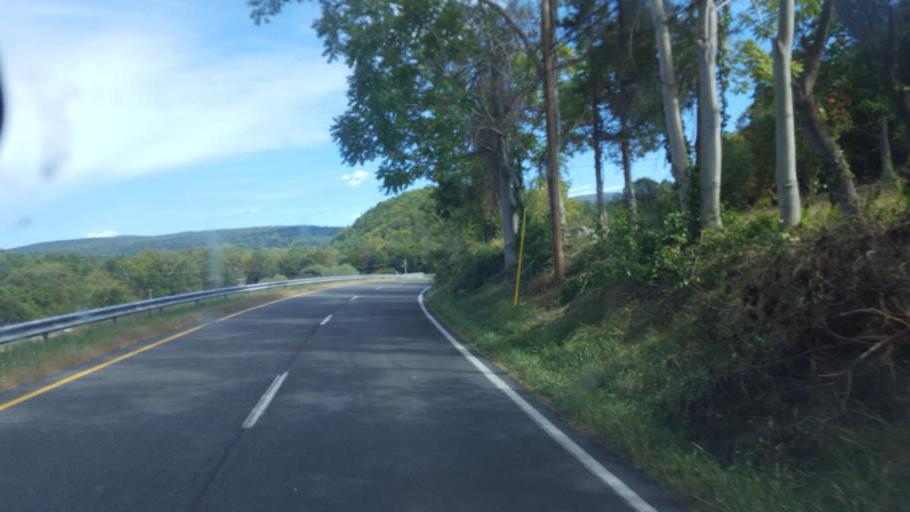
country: US
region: Virginia
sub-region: Page County
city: Luray
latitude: 38.6732
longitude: -78.3860
